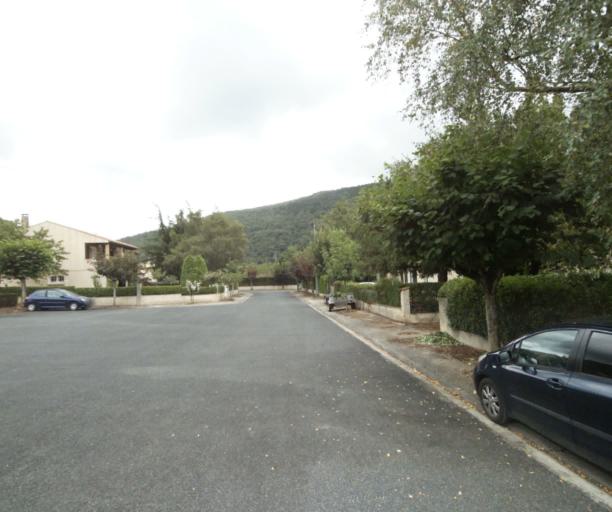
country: FR
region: Midi-Pyrenees
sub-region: Departement du Tarn
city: Soreze
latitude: 43.4443
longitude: 2.0602
